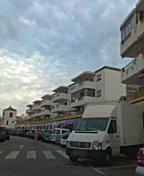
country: ES
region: Murcia
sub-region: Murcia
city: La Manga del Mar Menor
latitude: 37.6729
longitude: -0.7309
